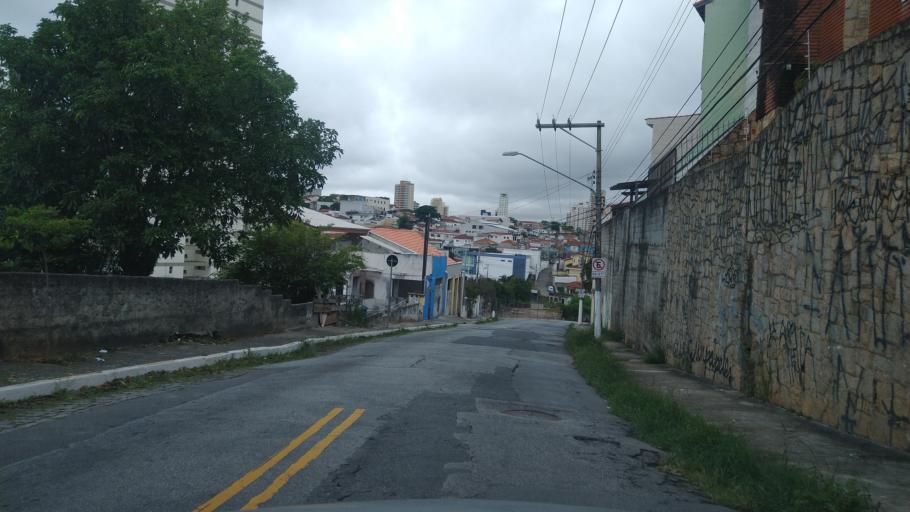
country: BR
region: Sao Paulo
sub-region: Sao Paulo
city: Sao Paulo
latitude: -23.4766
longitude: -46.6226
